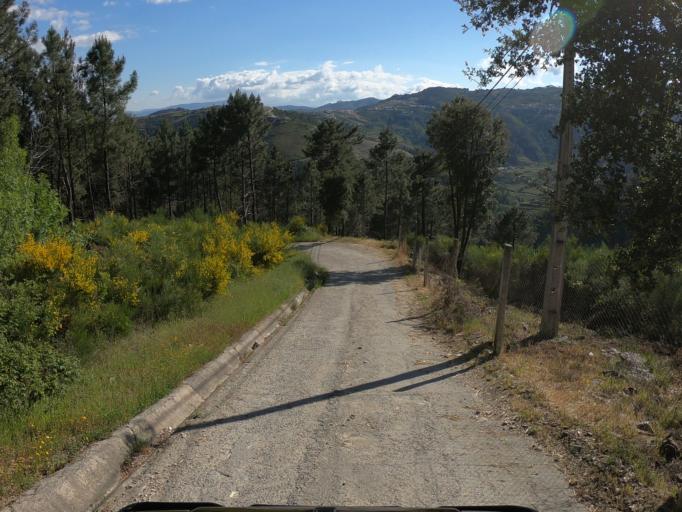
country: PT
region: Vila Real
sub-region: Vila Real
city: Vila Real
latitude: 41.2774
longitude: -7.7474
